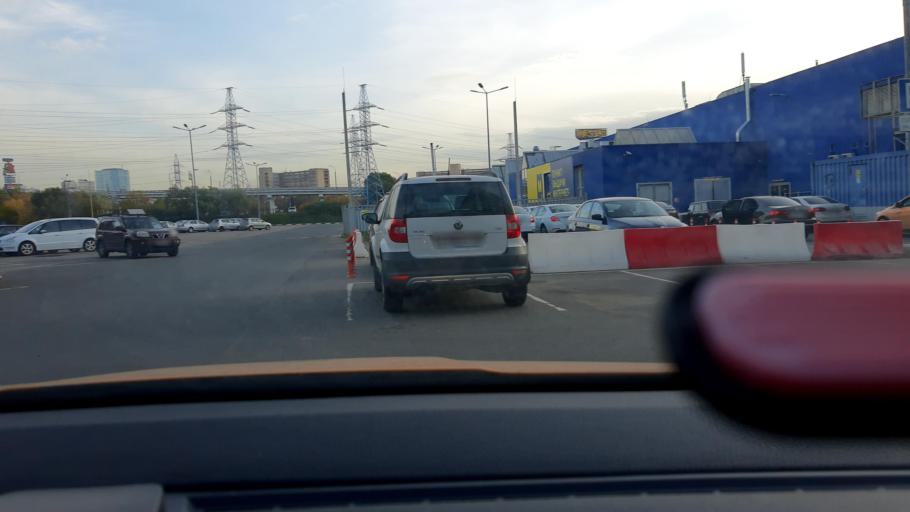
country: RU
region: Moscow
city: Khimki
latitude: 55.8761
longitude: 37.4451
